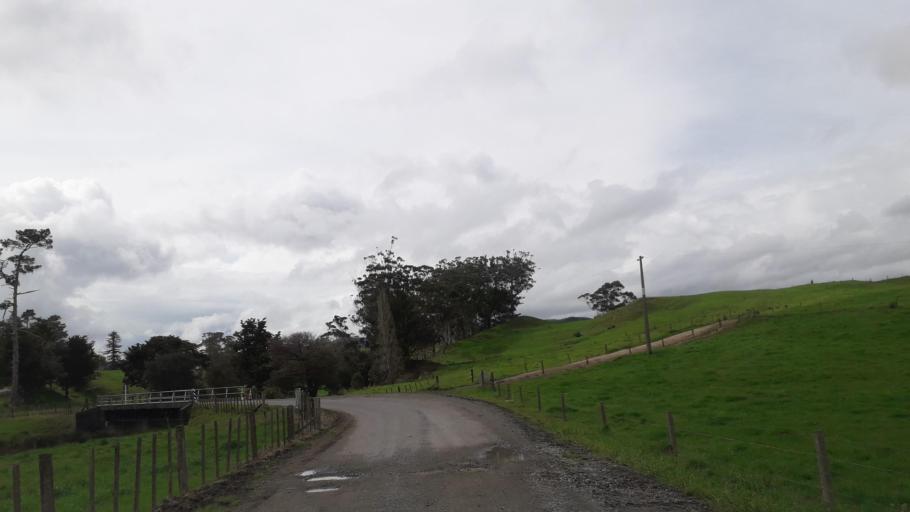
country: NZ
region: Northland
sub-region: Far North District
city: Waimate North
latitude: -35.2992
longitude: 173.5655
